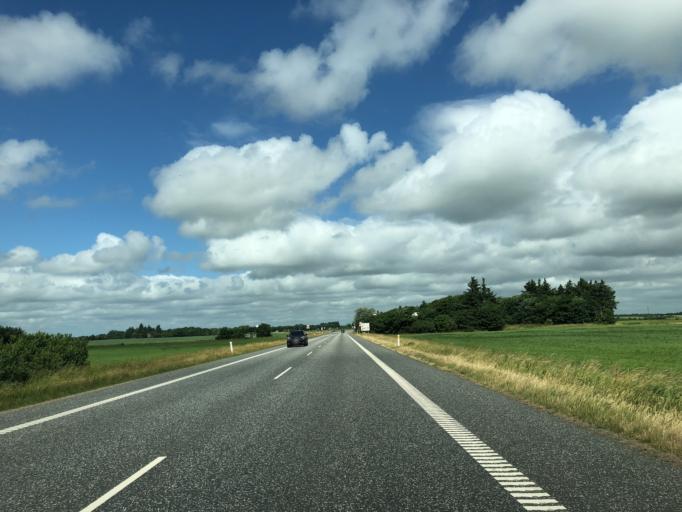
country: DK
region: Central Jutland
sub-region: Holstebro Kommune
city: Ulfborg
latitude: 56.2868
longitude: 8.3344
